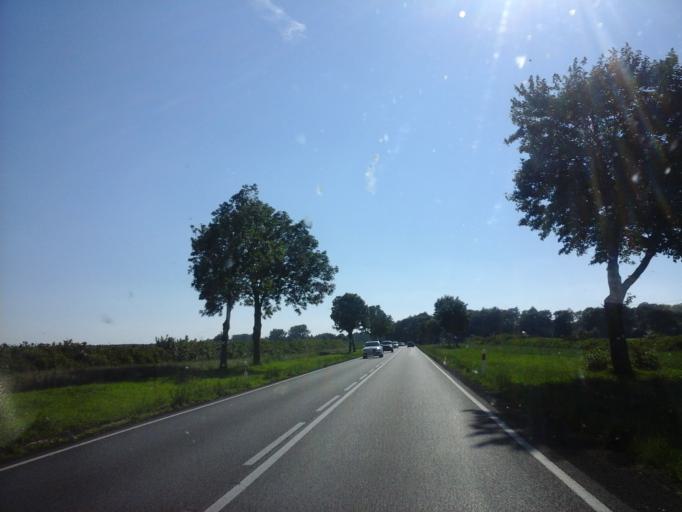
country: PL
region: West Pomeranian Voivodeship
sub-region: Powiat gryficki
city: Brojce
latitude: 53.8745
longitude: 15.3746
